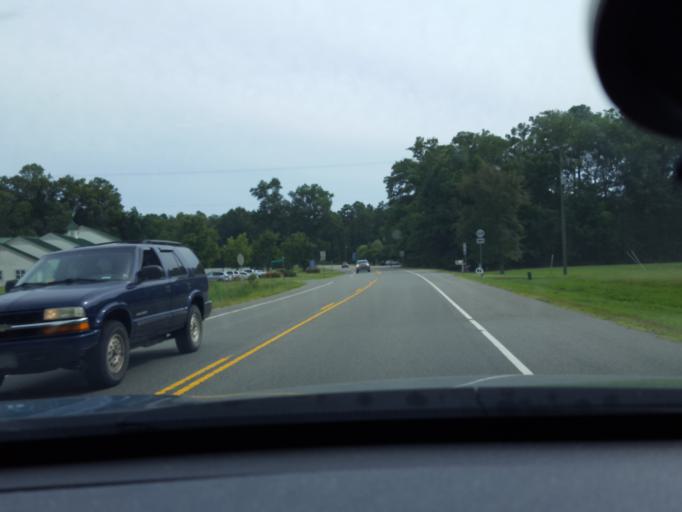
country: US
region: Virginia
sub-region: Hanover County
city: Hanover
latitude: 37.7708
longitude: -77.3713
